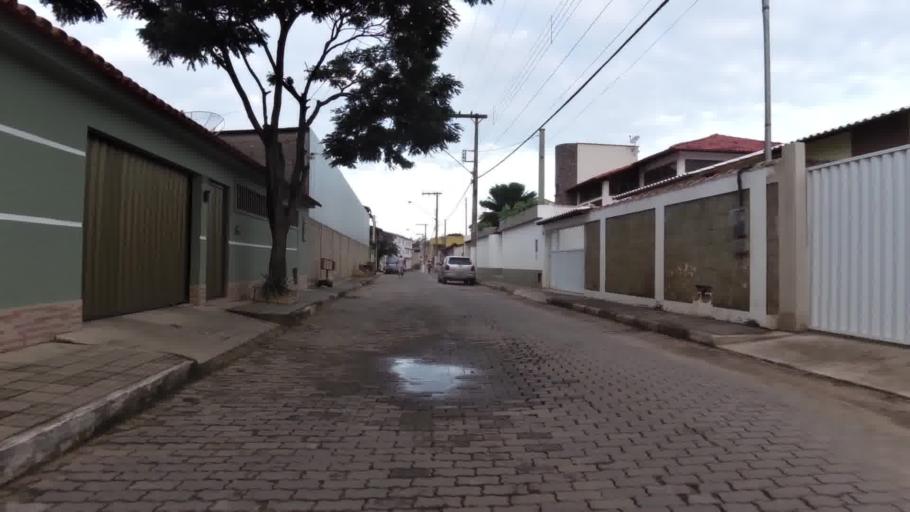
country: BR
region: Espirito Santo
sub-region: Piuma
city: Piuma
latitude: -20.8100
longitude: -40.6353
